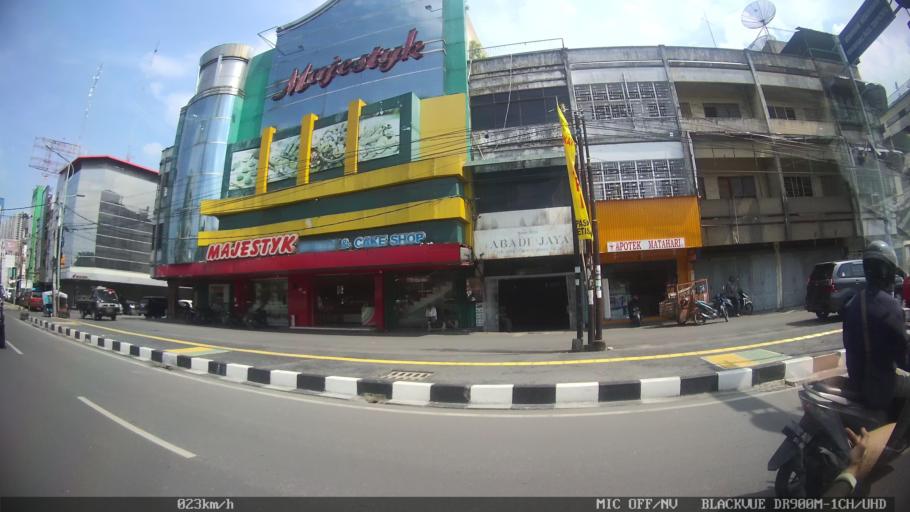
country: ID
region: North Sumatra
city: Medan
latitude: 3.5928
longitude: 98.6674
